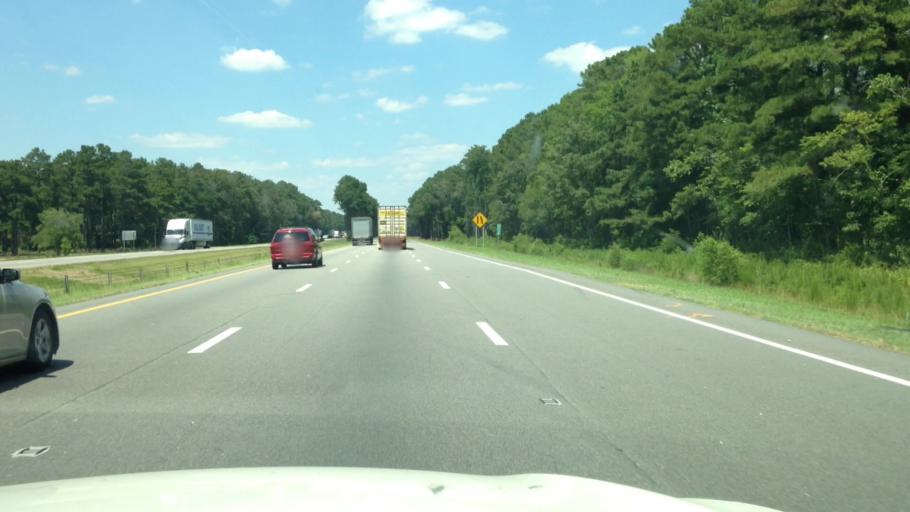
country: US
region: North Carolina
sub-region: Robeson County
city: Lumberton
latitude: 34.6759
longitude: -79.0040
